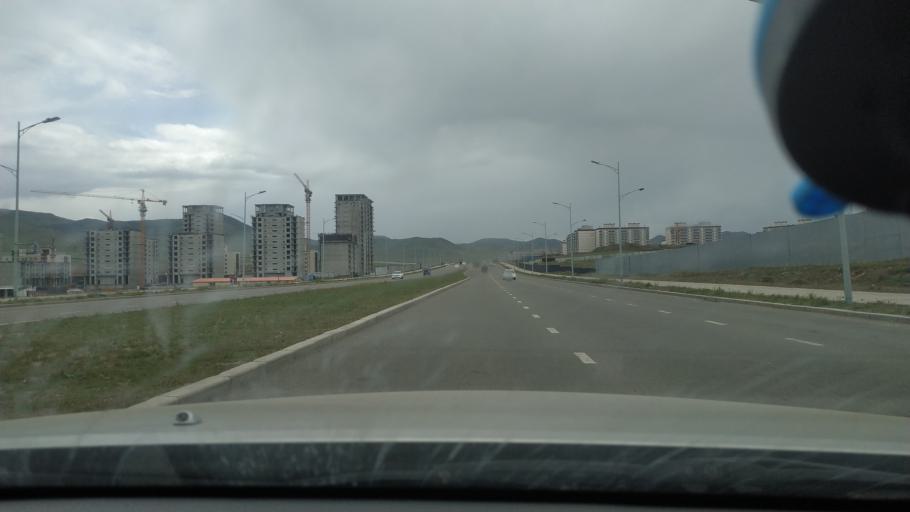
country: MN
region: Ulaanbaatar
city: Ulaanbaatar
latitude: 47.8524
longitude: 106.7885
